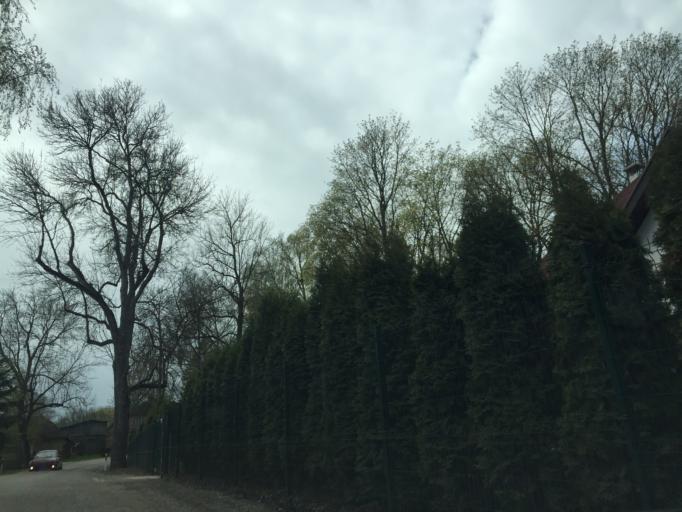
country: LV
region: Lecava
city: Iecava
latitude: 56.5923
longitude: 24.1968
